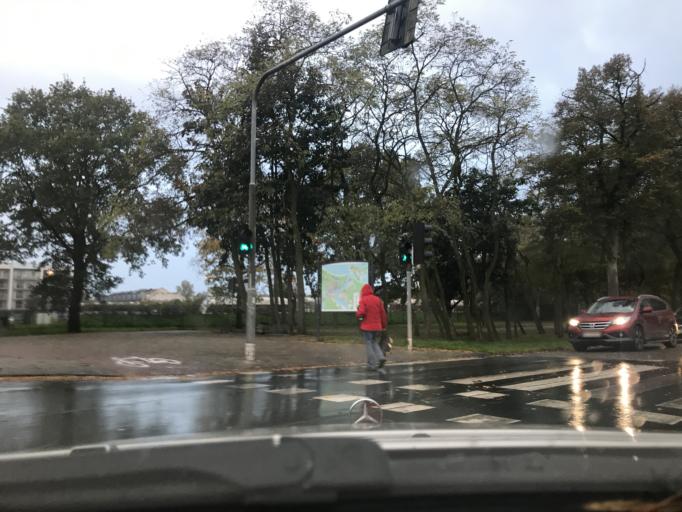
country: PL
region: West Pomeranian Voivodeship
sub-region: Swinoujscie
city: Swinoujscie
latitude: 53.9148
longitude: 14.2359
